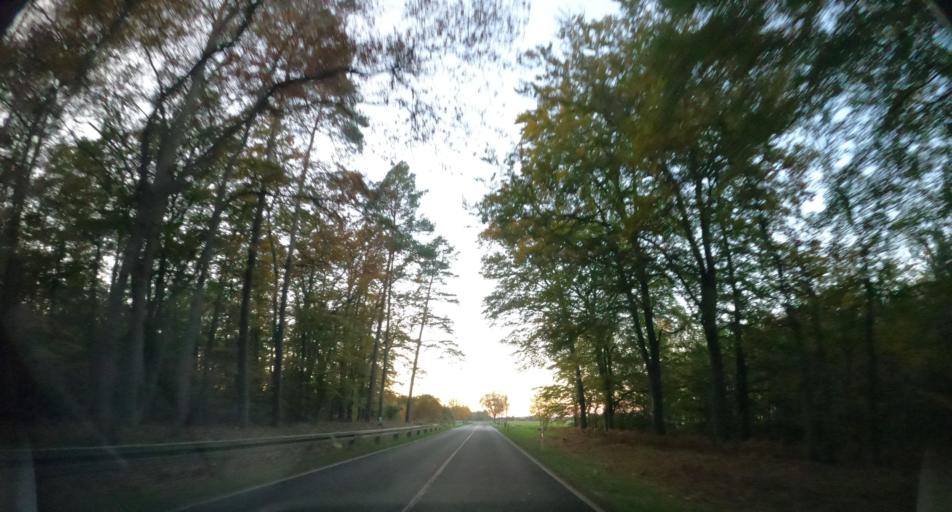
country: DE
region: Mecklenburg-Vorpommern
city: Usedom
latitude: 53.7683
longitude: 13.9210
